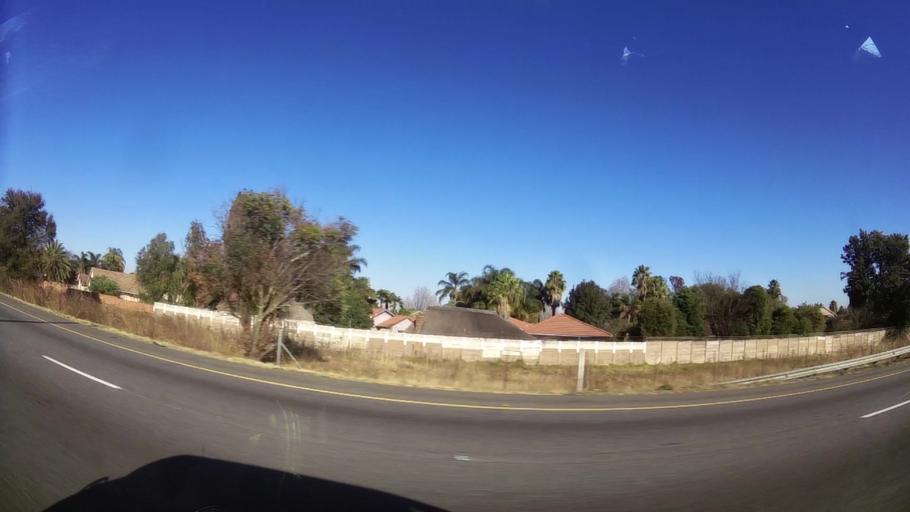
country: ZA
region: Gauteng
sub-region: City of Tshwane Metropolitan Municipality
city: Centurion
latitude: -25.8378
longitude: 28.2478
